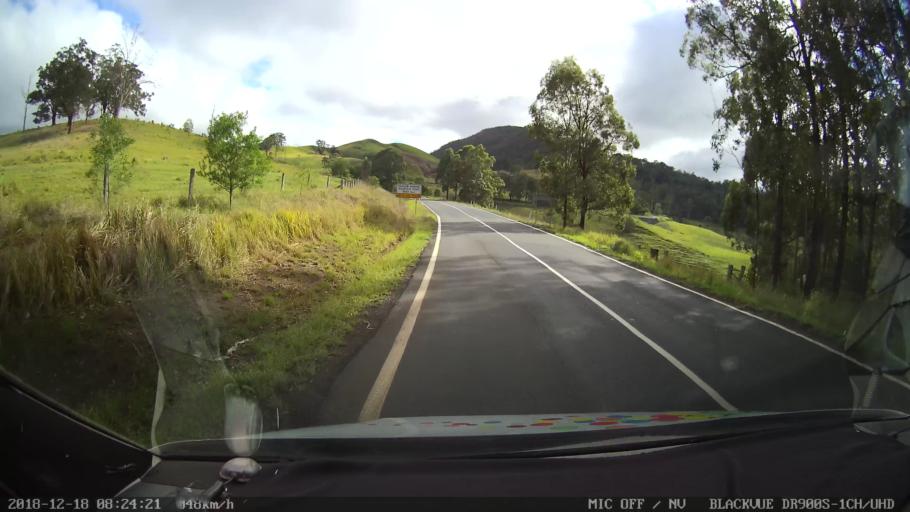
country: AU
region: New South Wales
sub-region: Kyogle
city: Kyogle
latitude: -28.3231
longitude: 152.7343
